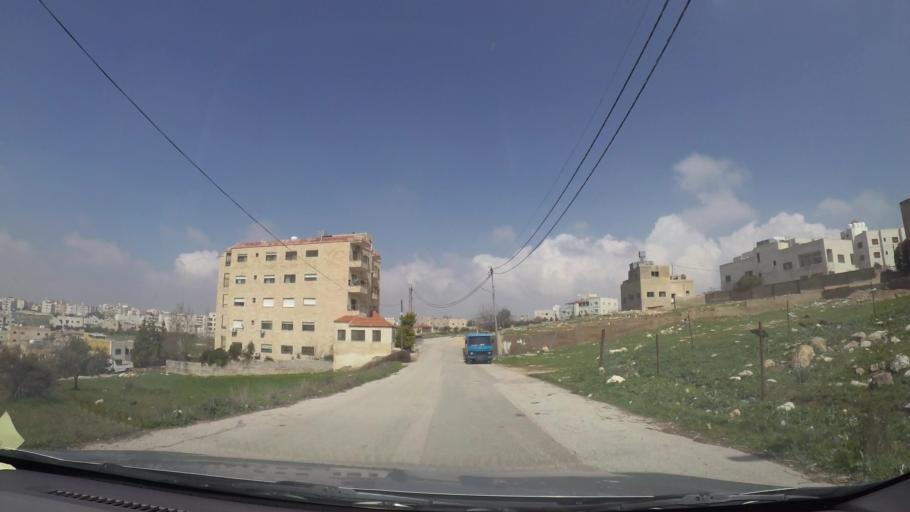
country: JO
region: Amman
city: Al Bunayyat ash Shamaliyah
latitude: 31.8914
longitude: 35.8913
